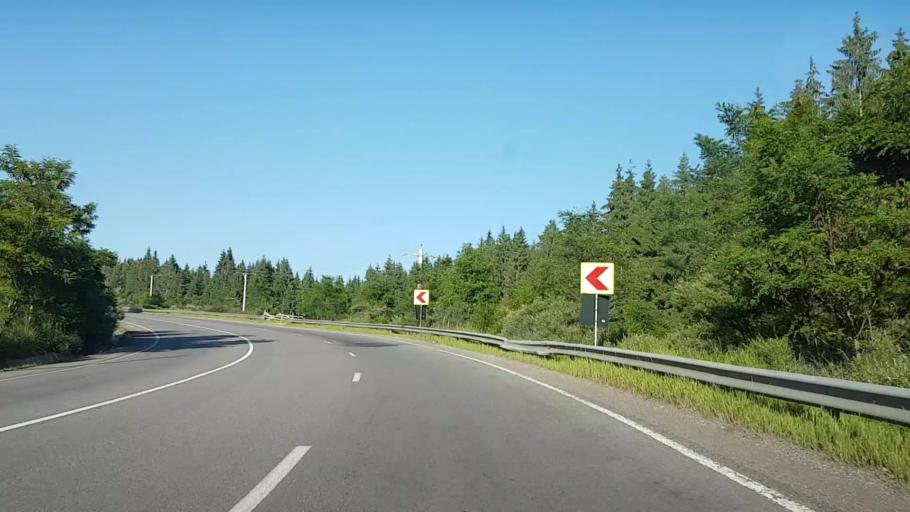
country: RO
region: Bistrita-Nasaud
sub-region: Comuna Lunca Ilvei
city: Lunca Ilvei
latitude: 47.2301
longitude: 24.9791
